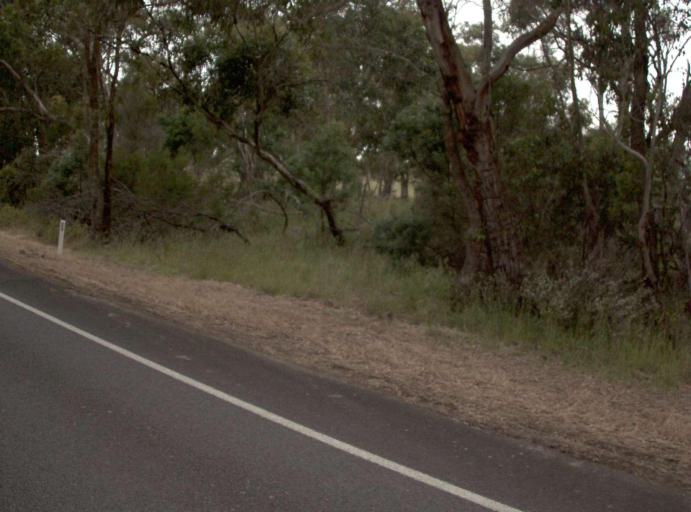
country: AU
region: Victoria
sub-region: Wellington
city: Sale
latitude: -38.4793
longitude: 146.9209
